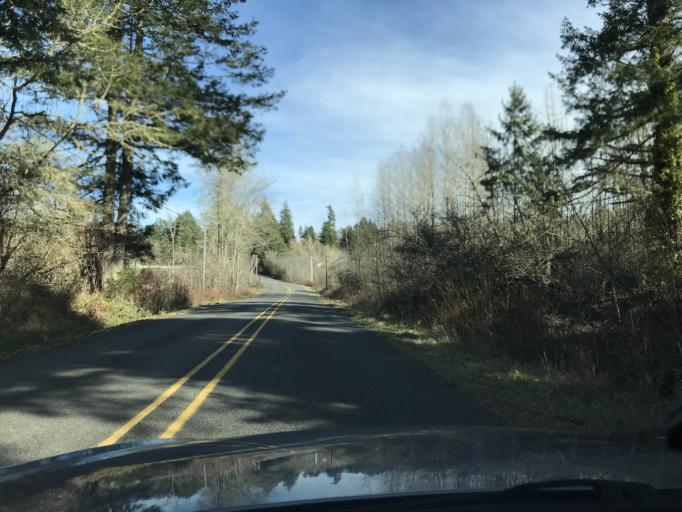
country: US
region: Washington
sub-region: Pierce County
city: Home
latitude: 47.2502
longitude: -122.7539
